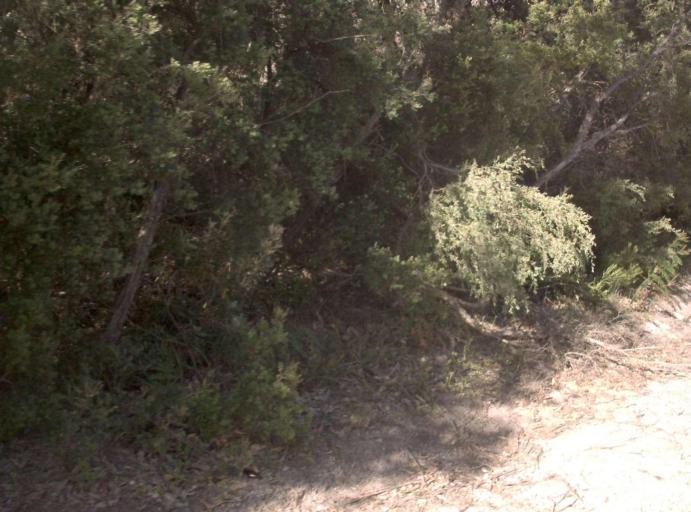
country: AU
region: Victoria
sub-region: East Gippsland
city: Lakes Entrance
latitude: -37.7976
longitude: 148.7019
